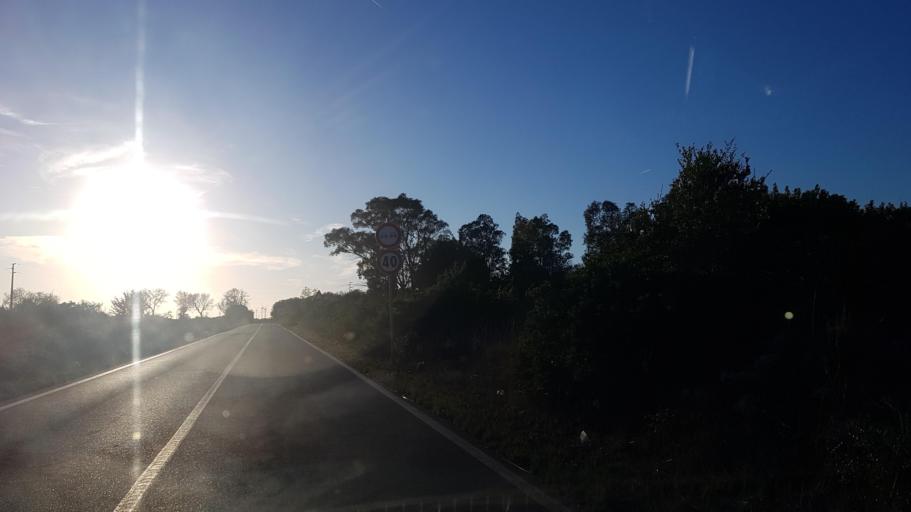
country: IT
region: Apulia
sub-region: Provincia di Lecce
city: Giorgilorio
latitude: 40.4189
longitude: 18.2162
